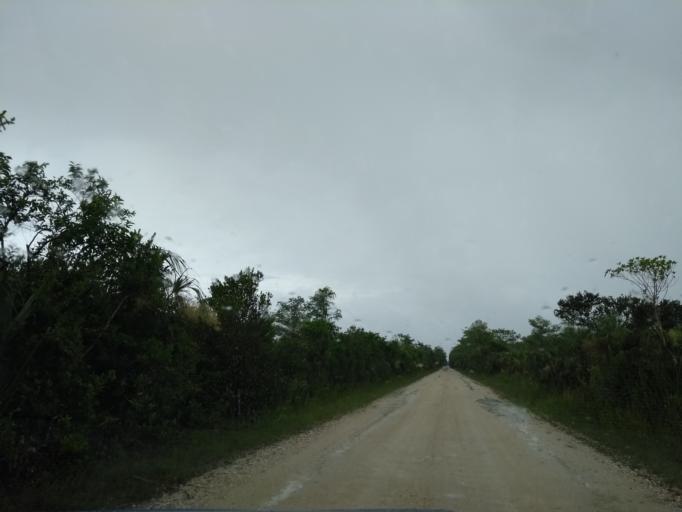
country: US
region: Florida
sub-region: Miami-Dade County
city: The Hammocks
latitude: 25.7602
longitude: -81.0333
